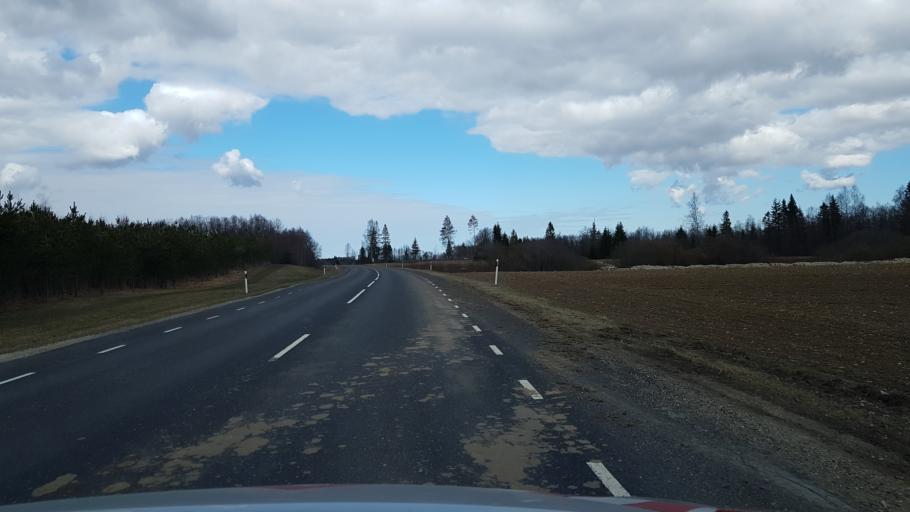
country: EE
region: Laeaene-Virumaa
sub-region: Rakvere linn
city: Rakvere
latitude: 59.2605
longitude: 26.2840
